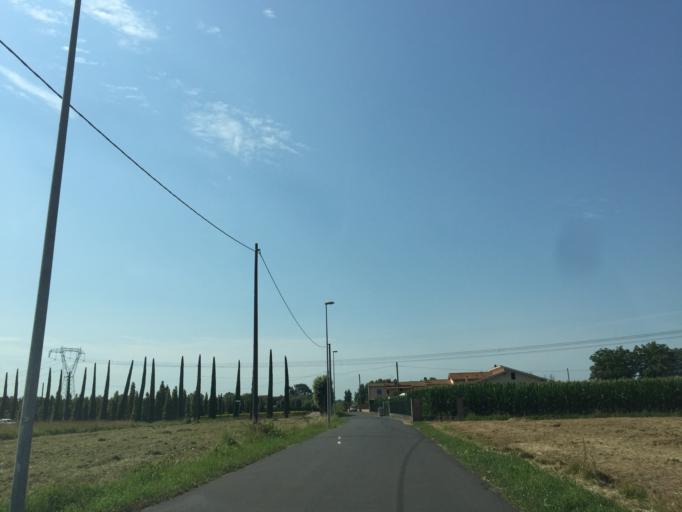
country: IT
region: Tuscany
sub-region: Provincia di Pistoia
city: Ponte Buggianese
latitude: 43.8612
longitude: 10.7558
